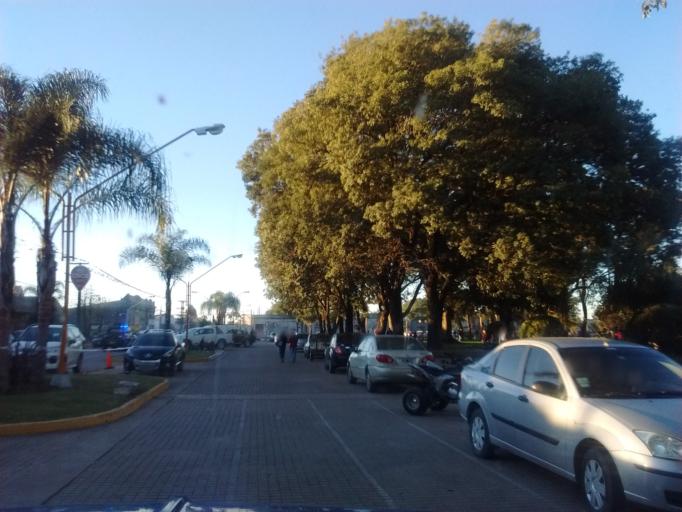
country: AR
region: Santa Fe
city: San Carlos Centro
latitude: -31.7609
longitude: -61.1012
